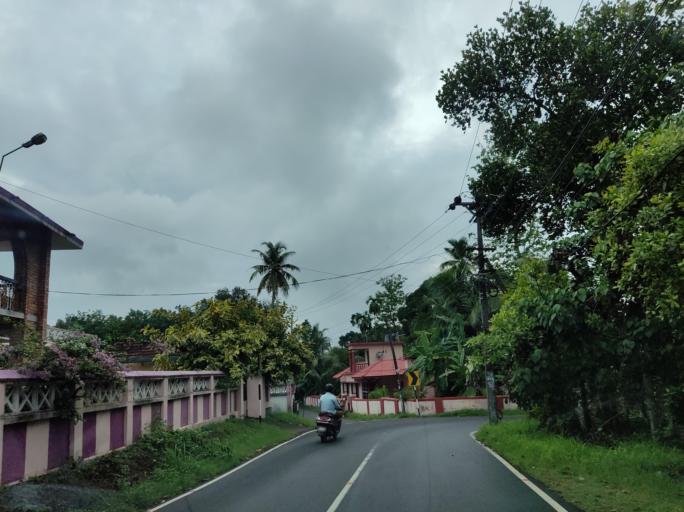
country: IN
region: Kerala
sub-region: Alappuzha
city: Mavelikara
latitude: 9.2382
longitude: 76.5538
